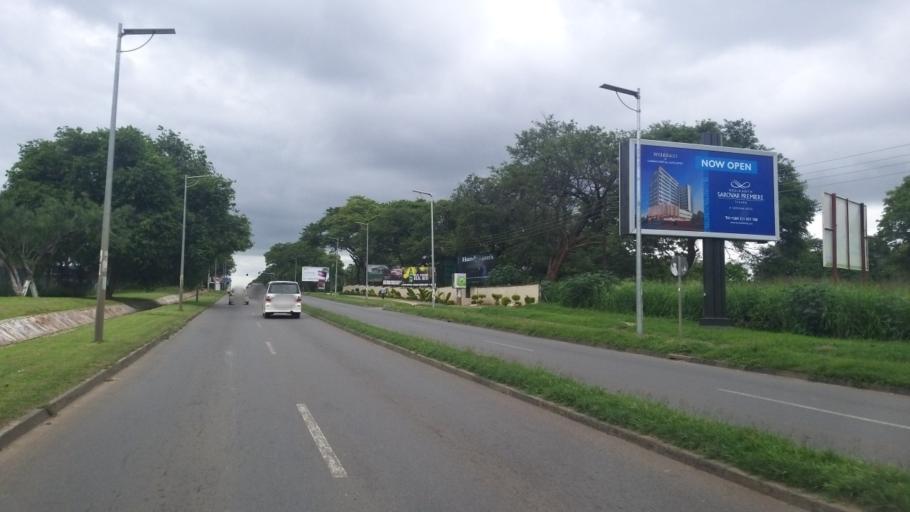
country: ZM
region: Lusaka
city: Lusaka
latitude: -15.4227
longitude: 28.3241
